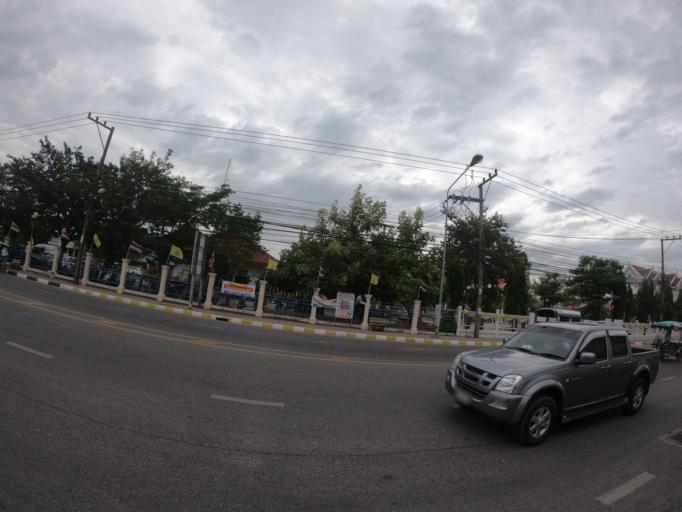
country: TH
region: Roi Et
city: Roi Et
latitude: 16.0537
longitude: 103.6543
